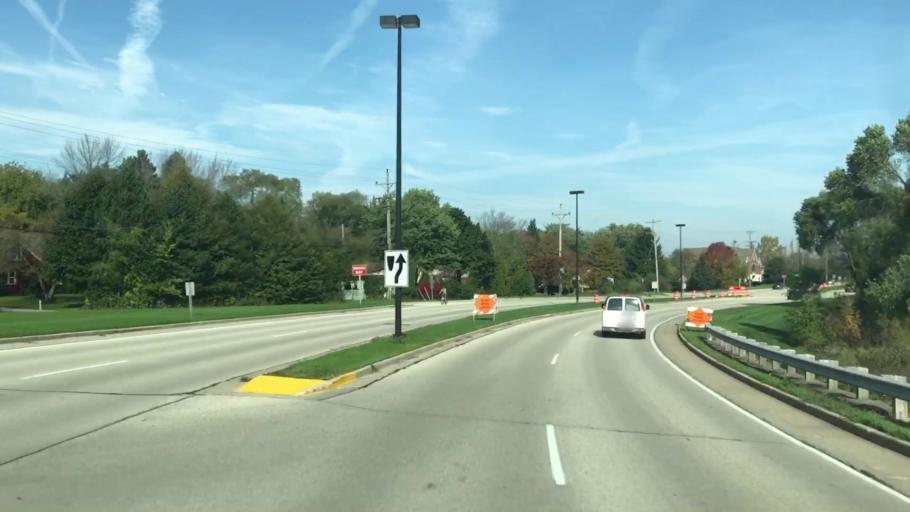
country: US
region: Wisconsin
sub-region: Milwaukee County
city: River Hills
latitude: 43.1979
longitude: -87.9239
